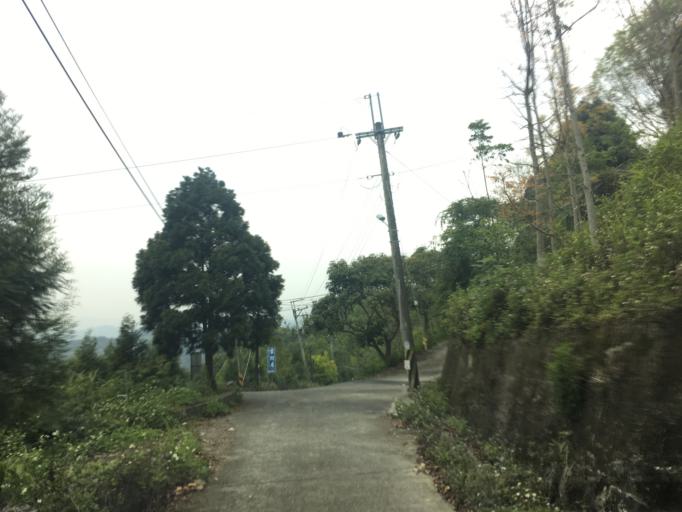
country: TW
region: Taiwan
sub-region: Taichung City
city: Taichung
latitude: 24.1463
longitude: 120.8239
